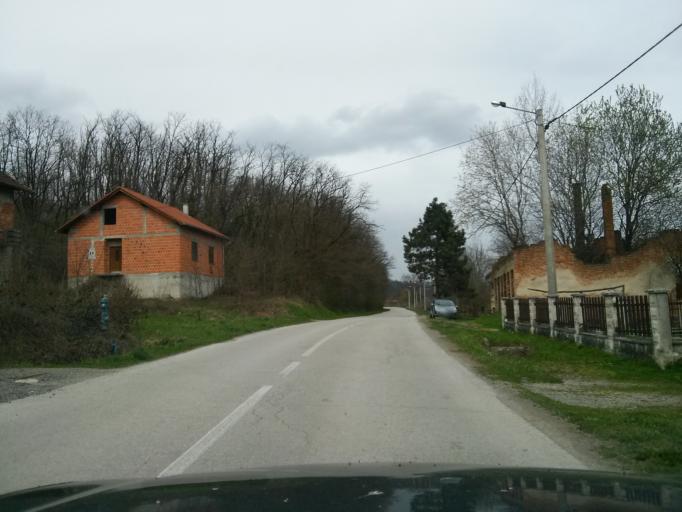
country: HR
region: Sisacko-Moslavacka
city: Gvozd
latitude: 45.2788
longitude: 15.9701
